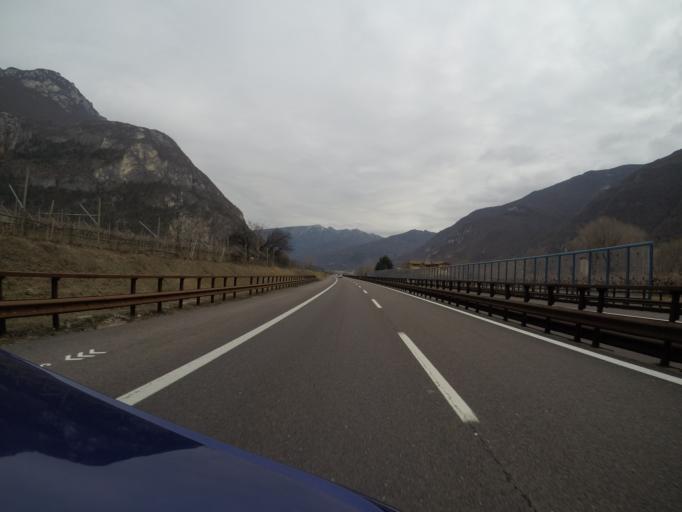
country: IT
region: Trentino-Alto Adige
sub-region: Provincia di Trento
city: Sabbionara
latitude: 45.7390
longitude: 10.9658
